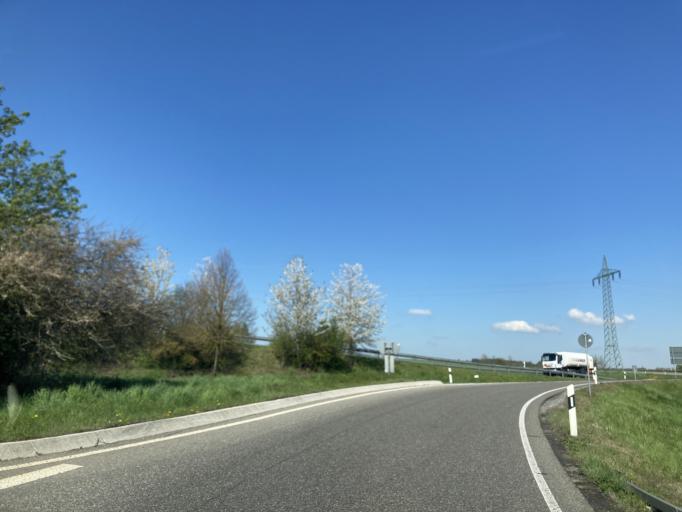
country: DE
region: Baden-Wuerttemberg
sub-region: Regierungsbezirk Stuttgart
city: Motzingen
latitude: 48.5060
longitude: 8.8006
